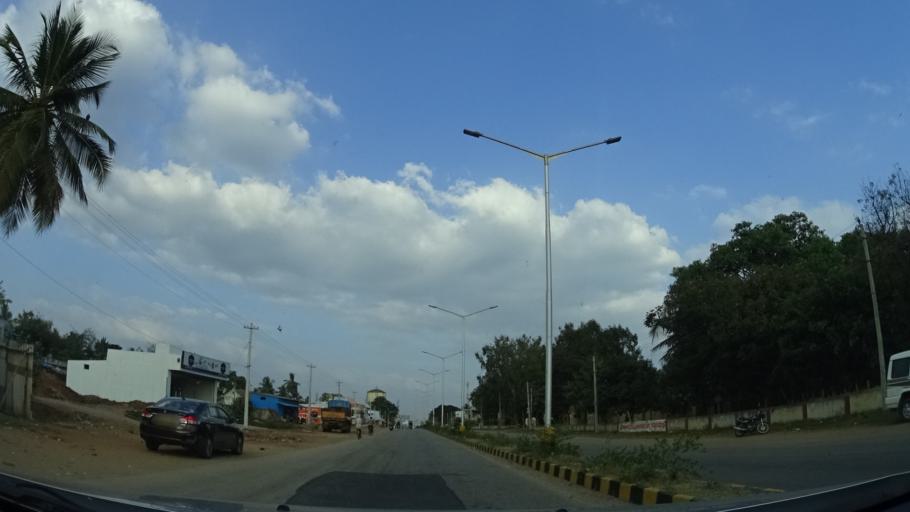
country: IN
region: Karnataka
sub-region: Mandya
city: Malavalli
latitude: 12.3818
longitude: 77.0477
